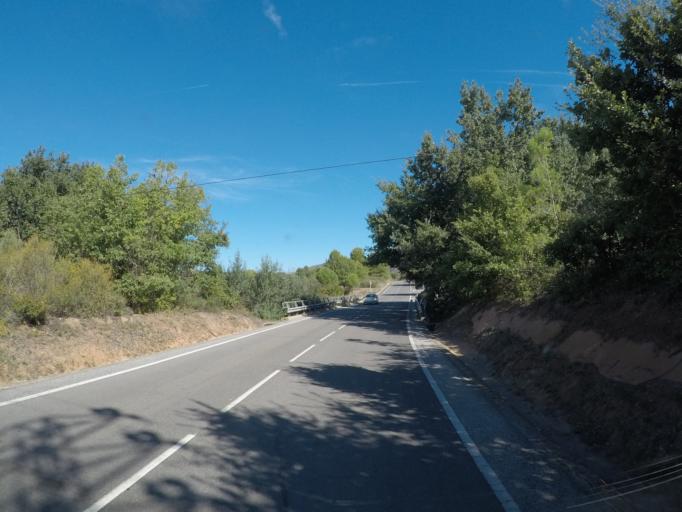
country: ES
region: Catalonia
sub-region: Provincia de Tarragona
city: Falset
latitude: 41.1508
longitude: 0.8177
